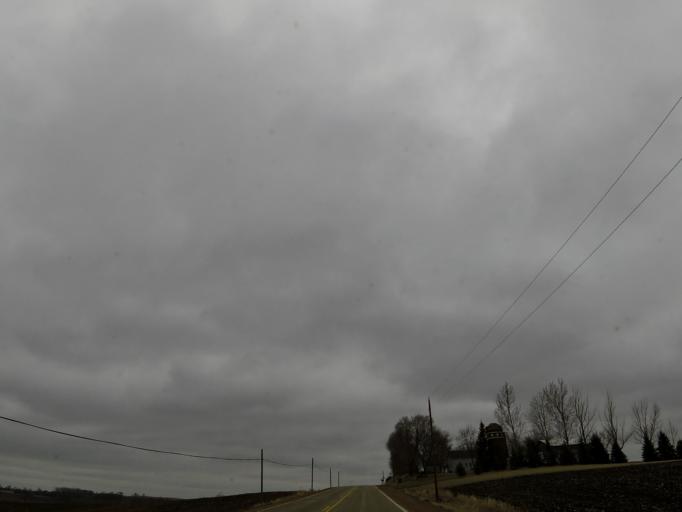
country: US
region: Minnesota
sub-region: Scott County
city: Shakopee
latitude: 44.7095
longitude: -93.5412
